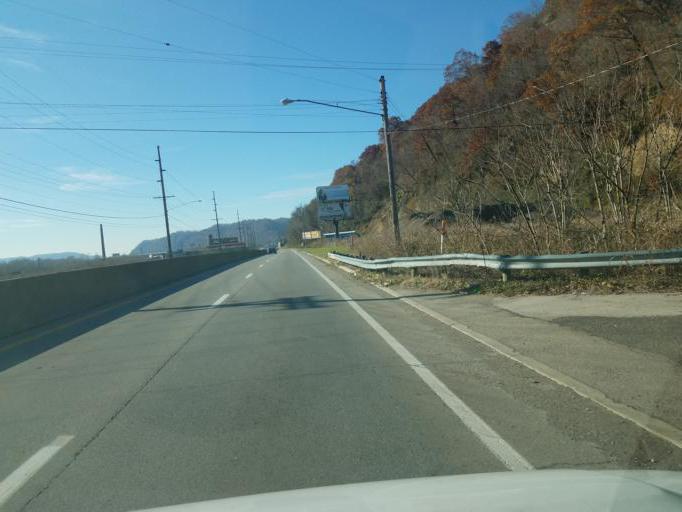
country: US
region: Ohio
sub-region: Scioto County
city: New Boston
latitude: 38.7554
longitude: -82.9114
